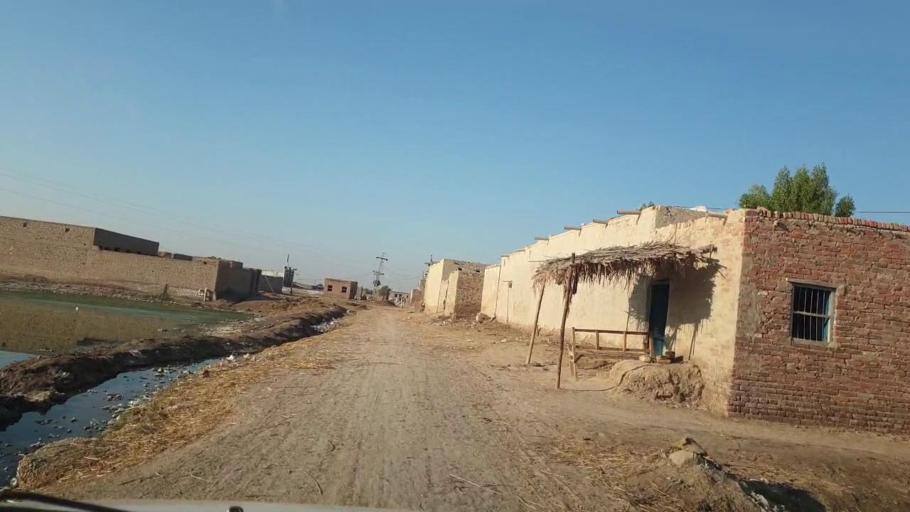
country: PK
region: Sindh
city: Khairpur Nathan Shah
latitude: 27.0471
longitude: 67.7247
